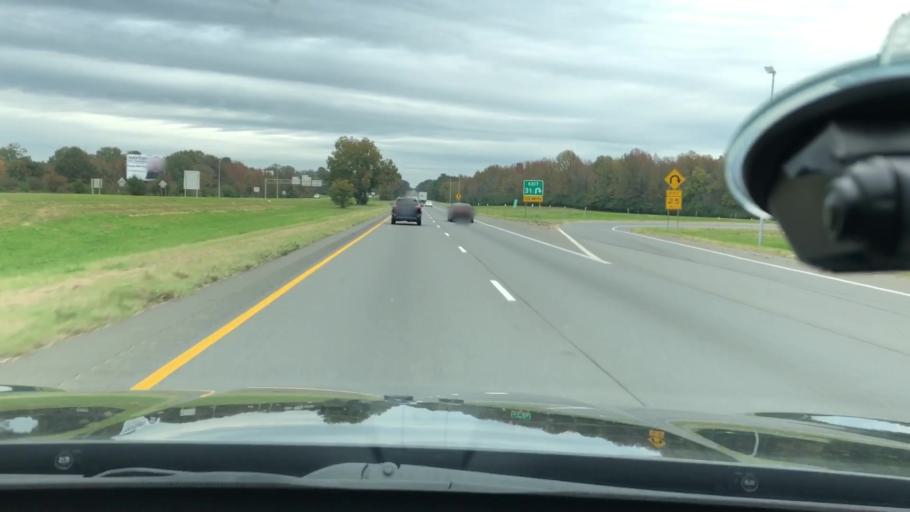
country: US
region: Arkansas
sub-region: Hempstead County
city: Hope
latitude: 33.6914
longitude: -93.5974
